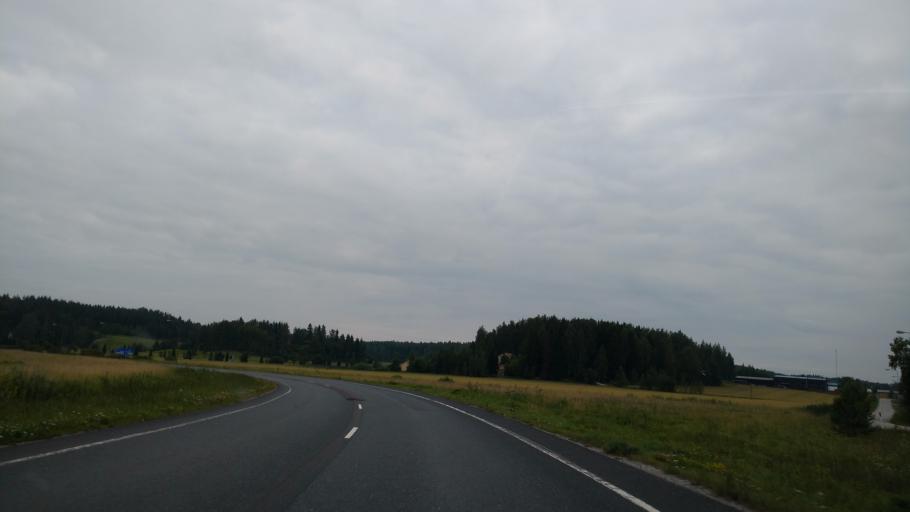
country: FI
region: Varsinais-Suomi
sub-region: Salo
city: Halikko
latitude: 60.3886
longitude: 23.0503
